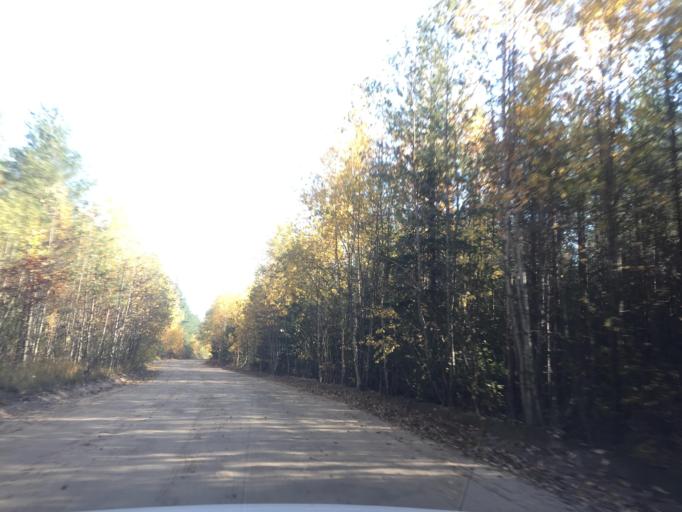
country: RU
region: Leningrad
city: Kuznechnoye
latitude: 61.3109
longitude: 30.0262
